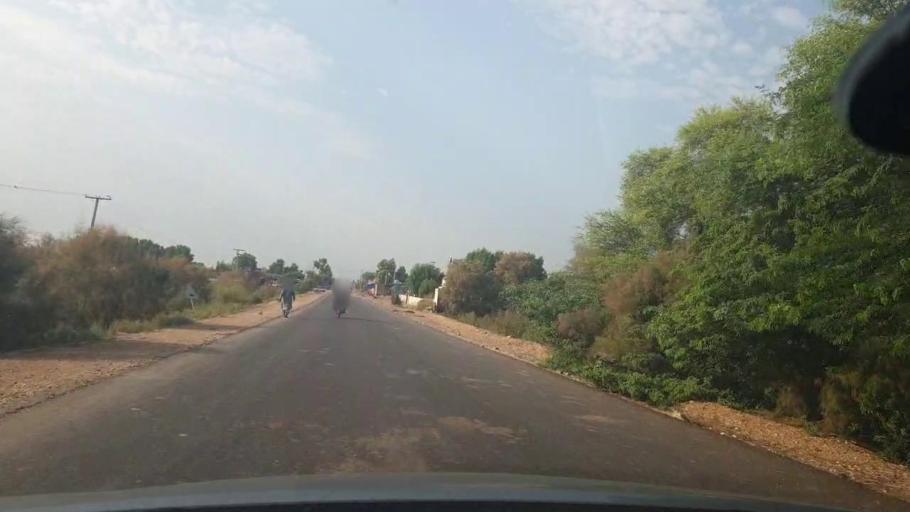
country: PK
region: Sindh
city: Jacobabad
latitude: 28.1107
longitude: 68.3265
